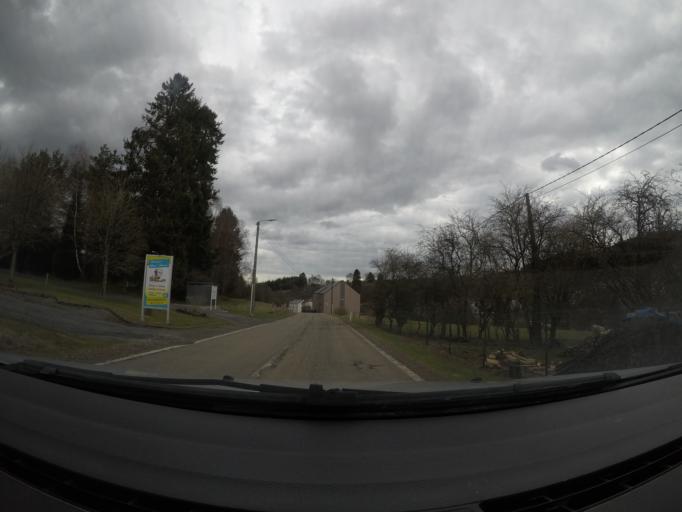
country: BE
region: Wallonia
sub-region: Province du Luxembourg
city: Leglise
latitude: 49.7646
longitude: 5.5103
